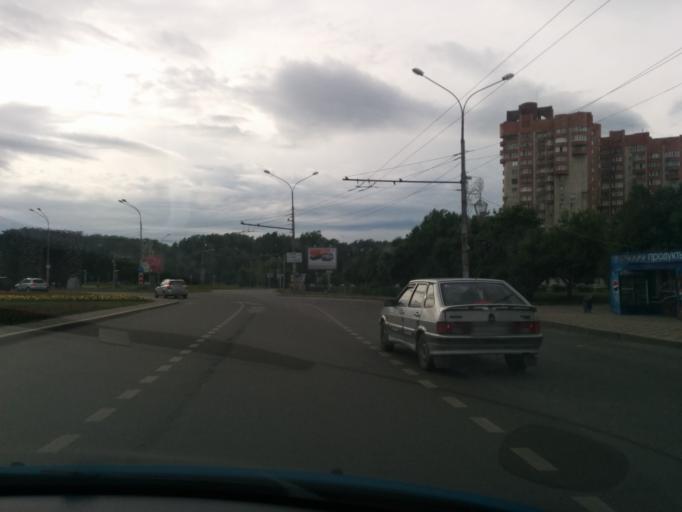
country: RU
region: Perm
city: Perm
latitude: 58.0041
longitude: 56.1959
